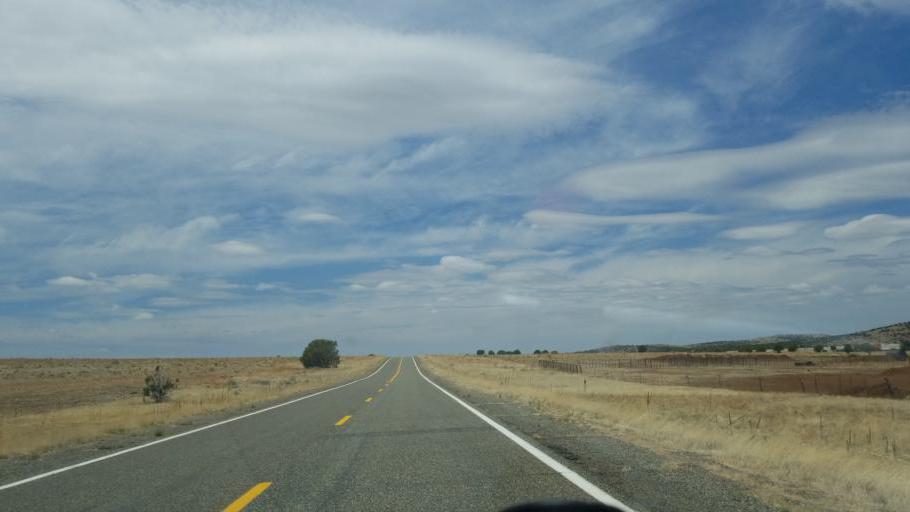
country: US
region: Arizona
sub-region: Yavapai County
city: Paulden
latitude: 35.2856
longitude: -112.7229
